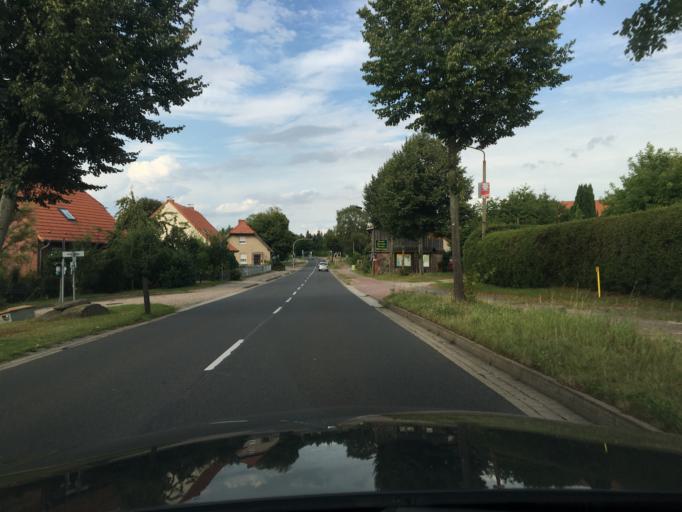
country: DE
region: Mecklenburg-Vorpommern
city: Wustrow
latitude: 53.4413
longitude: 13.1771
